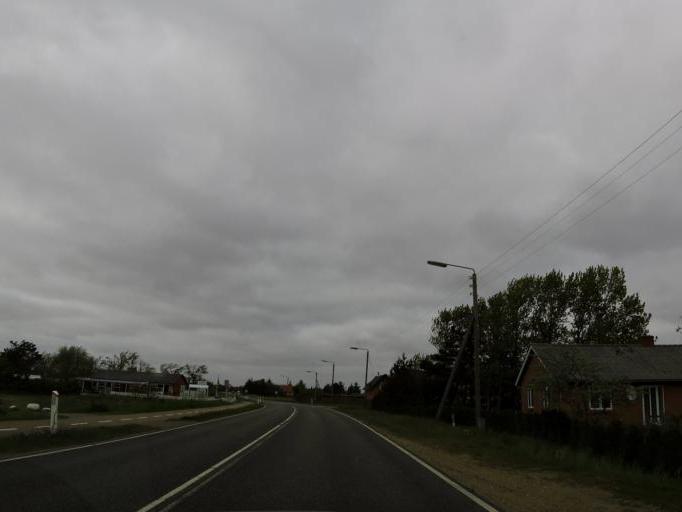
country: DE
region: Schleswig-Holstein
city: List
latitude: 55.1335
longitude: 8.5500
